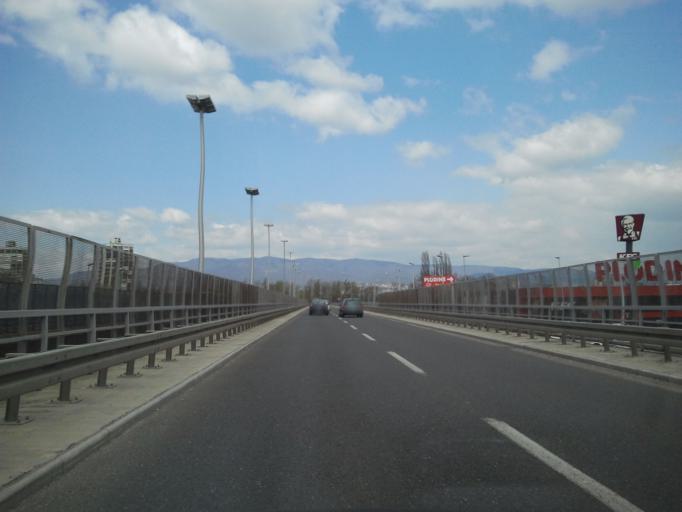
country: HR
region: Grad Zagreb
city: Novi Zagreb
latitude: 45.7775
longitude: 16.0024
